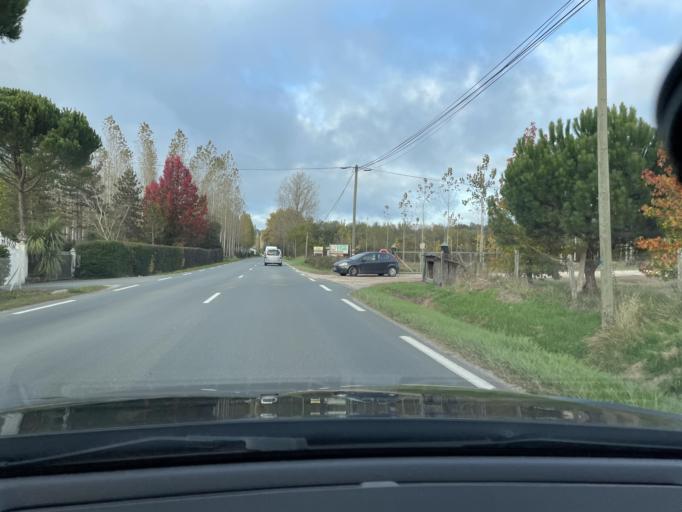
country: FR
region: Aquitaine
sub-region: Departement du Lot-et-Garonne
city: Casteljaloux
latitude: 44.3349
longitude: 0.1021
